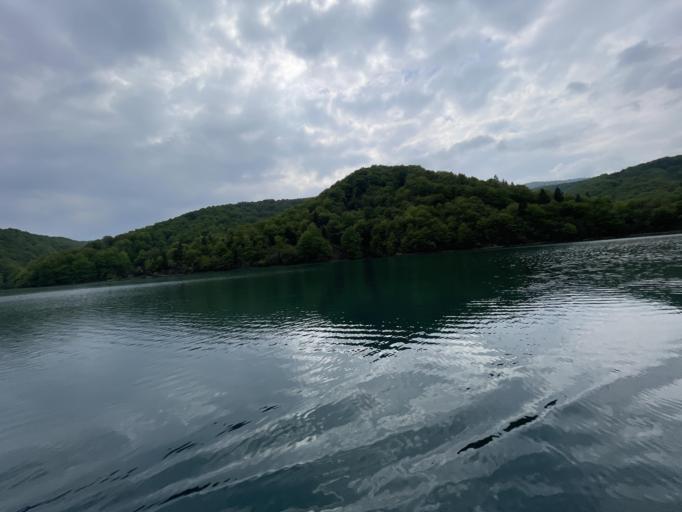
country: HR
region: Licko-Senjska
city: Jezerce
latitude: 44.8901
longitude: 15.6056
